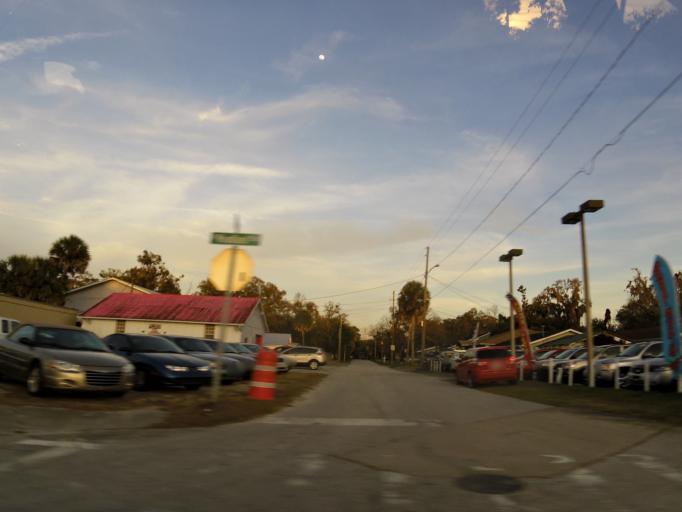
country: US
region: Florida
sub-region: Volusia County
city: North DeLand
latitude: 29.0474
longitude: -81.3040
